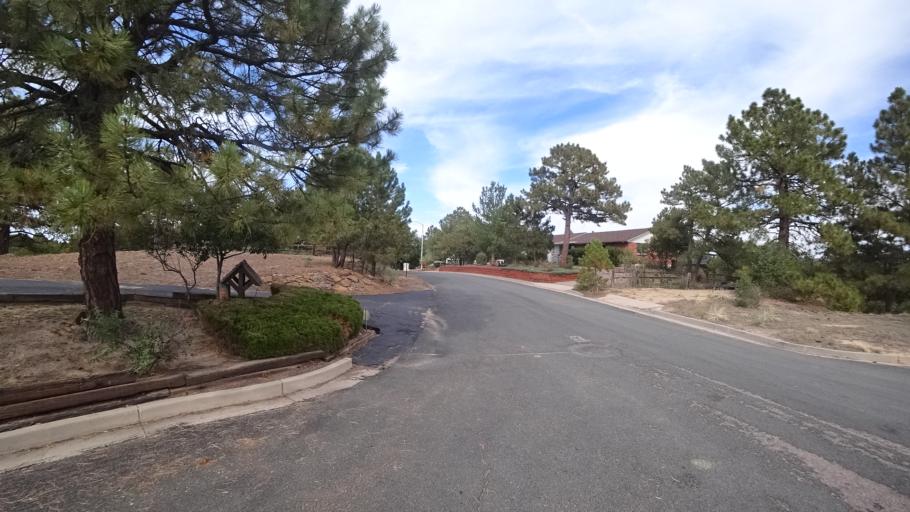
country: US
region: Colorado
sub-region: El Paso County
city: Colorado Springs
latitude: 38.8934
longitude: -104.7760
